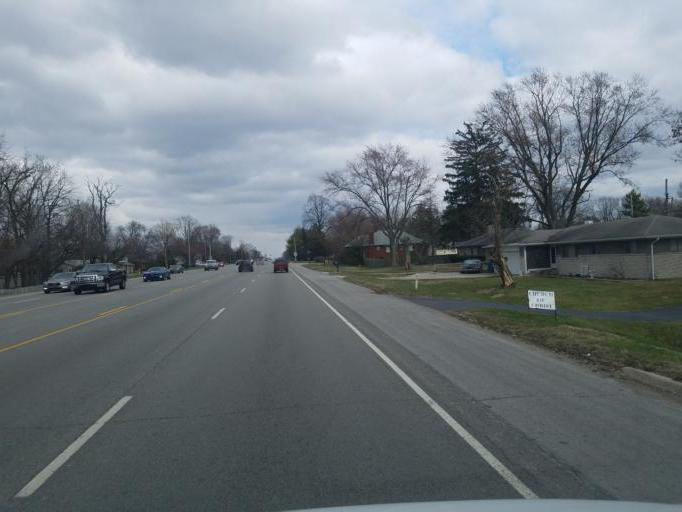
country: US
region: Indiana
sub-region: Marion County
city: Speedway
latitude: 39.7643
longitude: -86.2860
